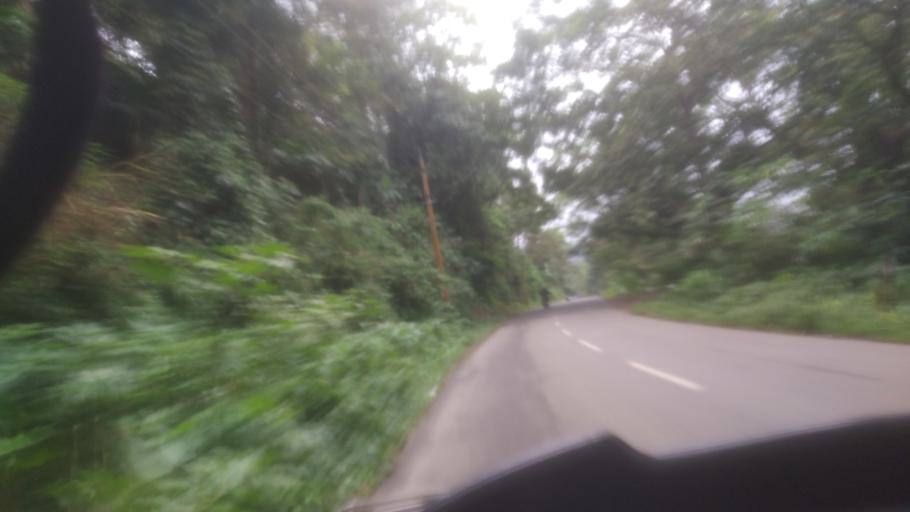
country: IN
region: Tamil Nadu
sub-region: Theni
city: Kombai
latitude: 9.8966
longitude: 77.1937
